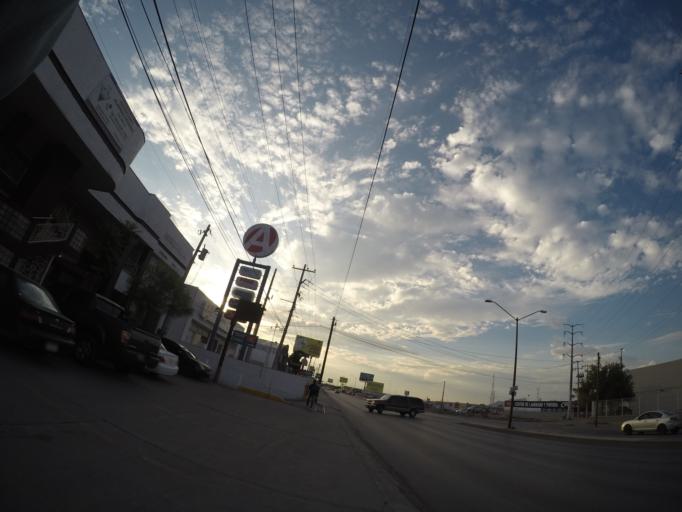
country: MX
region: Chihuahua
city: Ciudad Juarez
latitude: 31.7037
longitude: -106.4193
